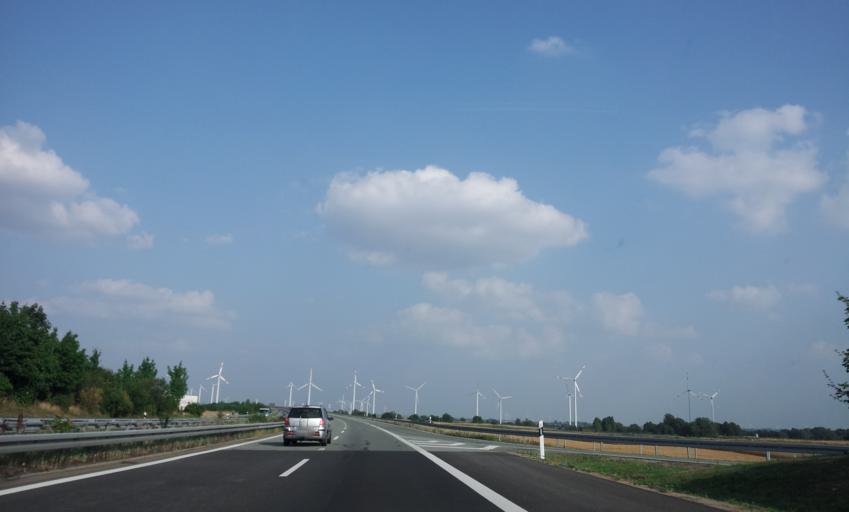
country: DE
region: Mecklenburg-Vorpommern
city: Strasburg
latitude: 53.5203
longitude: 13.7781
